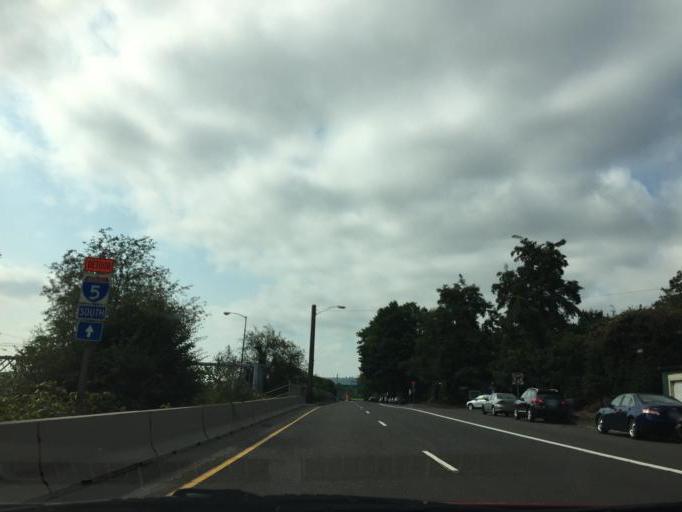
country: US
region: Oregon
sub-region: Multnomah County
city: Portland
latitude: 45.4985
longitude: -122.6738
